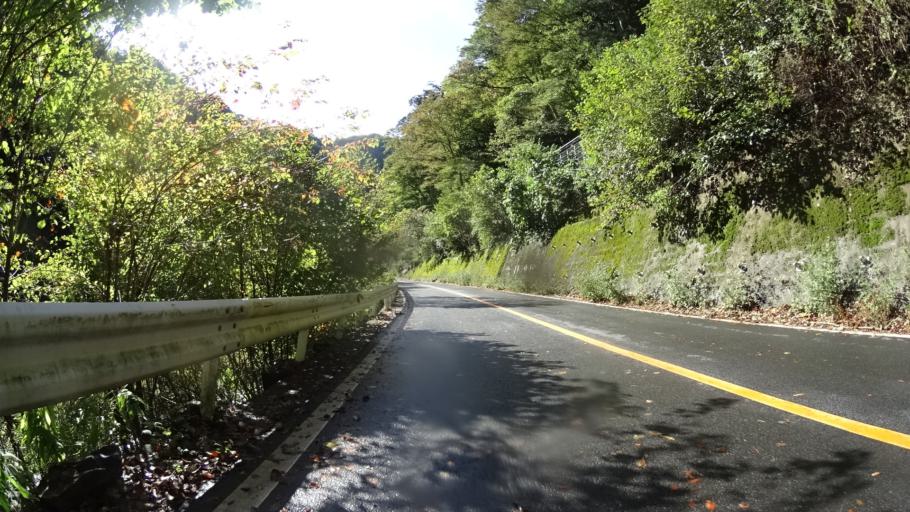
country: JP
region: Yamanashi
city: Enzan
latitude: 35.8065
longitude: 138.8539
